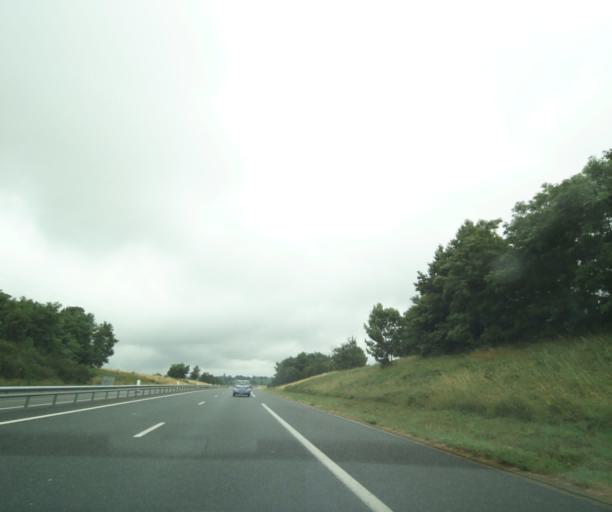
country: FR
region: Midi-Pyrenees
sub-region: Departement de l'Aveyron
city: Luc-la-Primaube
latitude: 44.2979
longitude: 2.5236
